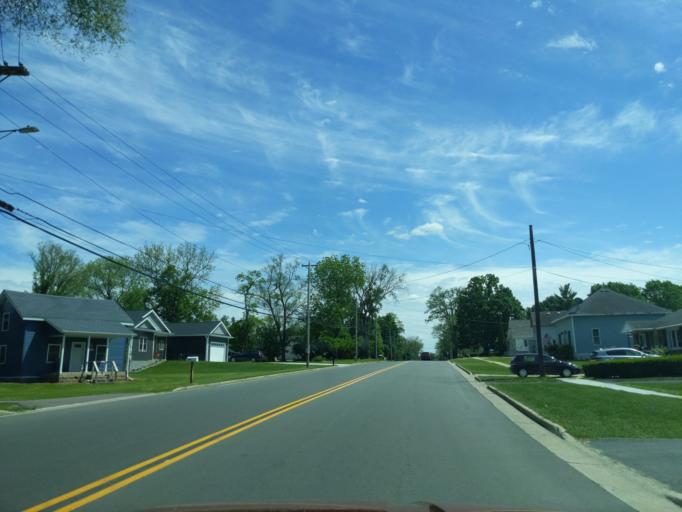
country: US
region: Wisconsin
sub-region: Columbia County
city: Pardeeville
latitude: 43.5441
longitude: -89.3028
